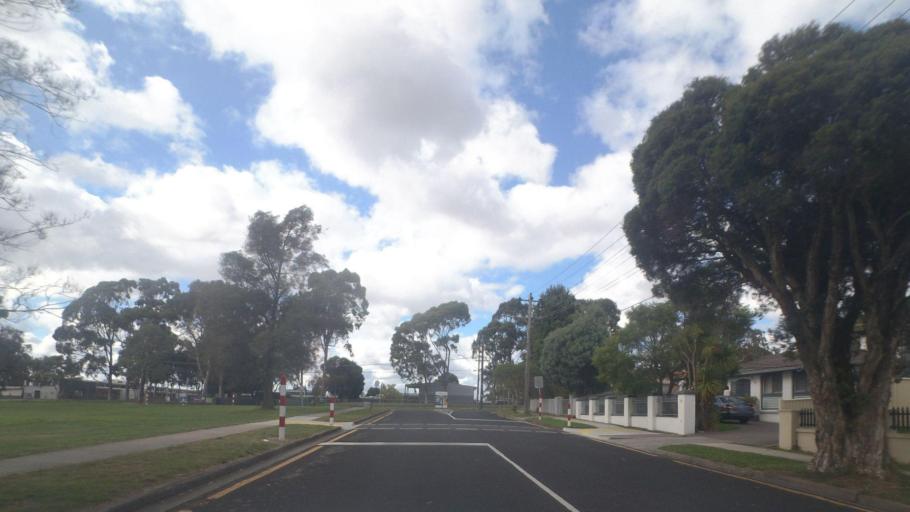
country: AU
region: Victoria
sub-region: Whitehorse
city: Vermont South
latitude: -37.8530
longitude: 145.1797
